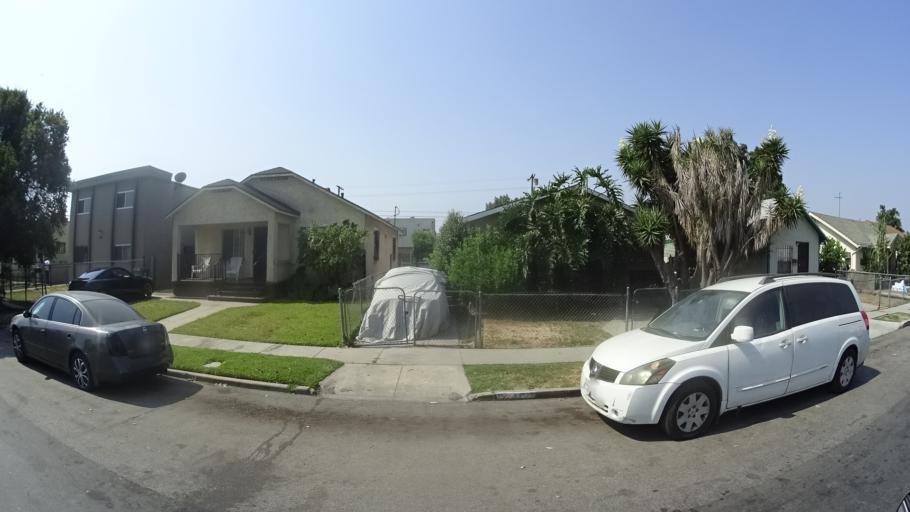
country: US
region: California
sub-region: Los Angeles County
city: Westmont
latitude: 33.9737
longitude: -118.2902
